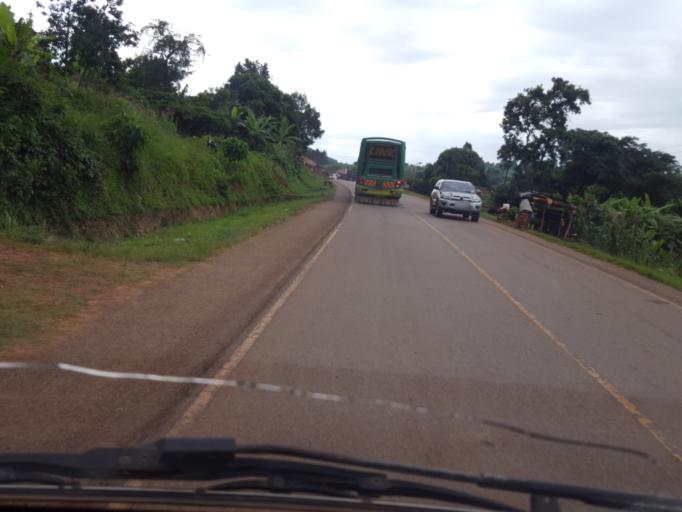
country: UG
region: Central Region
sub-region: Mityana District
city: Mityana
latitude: 0.6725
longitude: 32.0838
